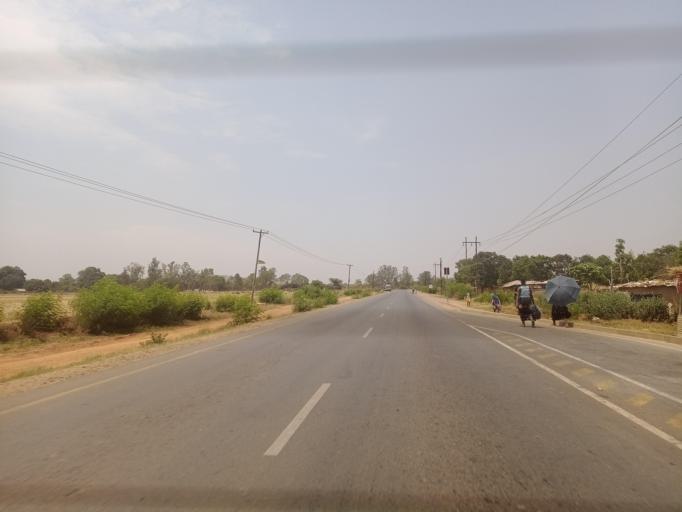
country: ZM
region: Lusaka
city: Lusaka
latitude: -15.2741
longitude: 28.4058
